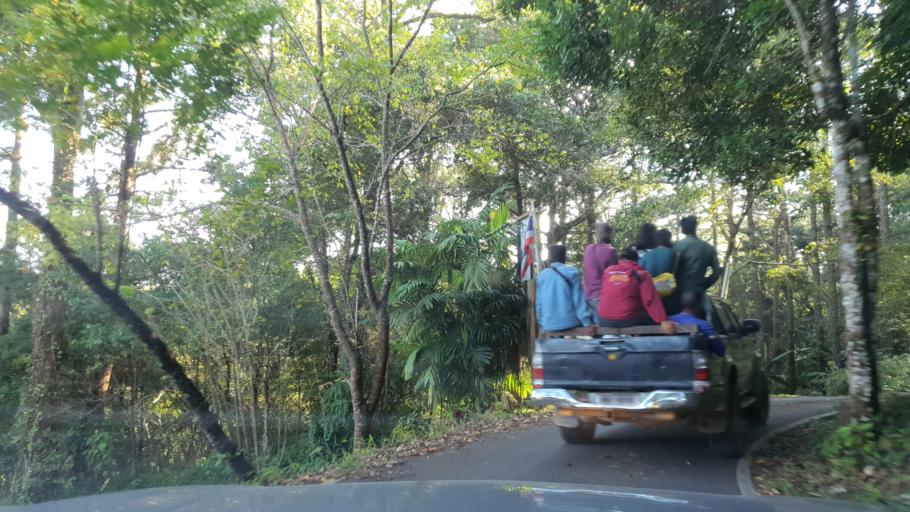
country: TH
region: Chiang Mai
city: Chiang Mai
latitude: 18.8257
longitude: 98.8938
